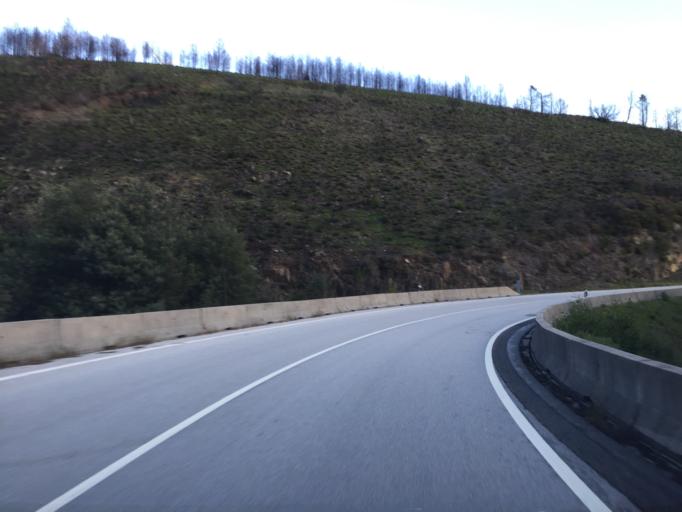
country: PT
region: Coimbra
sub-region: Pampilhosa da Serra
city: Pampilhosa da Serra
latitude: 40.0971
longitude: -7.9874
